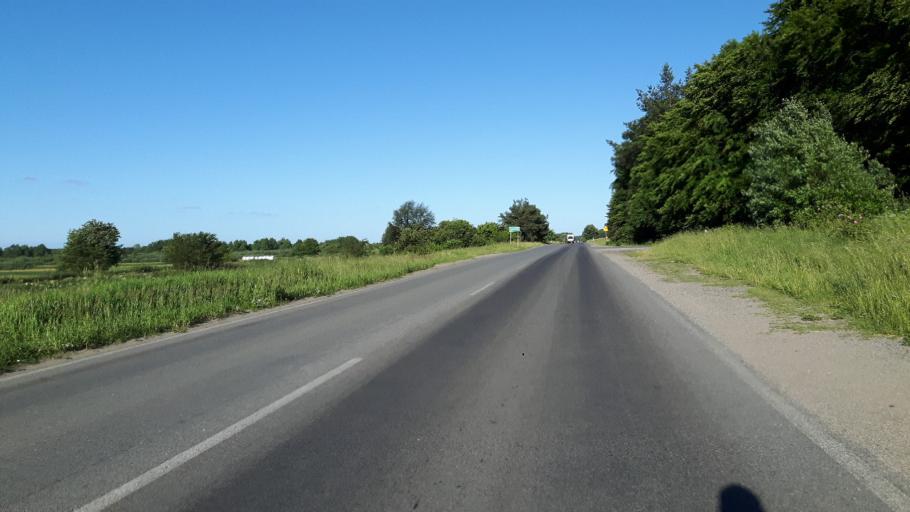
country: PL
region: Pomeranian Voivodeship
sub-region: Powiat pucki
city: Mrzezino
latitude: 54.6051
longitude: 18.4258
